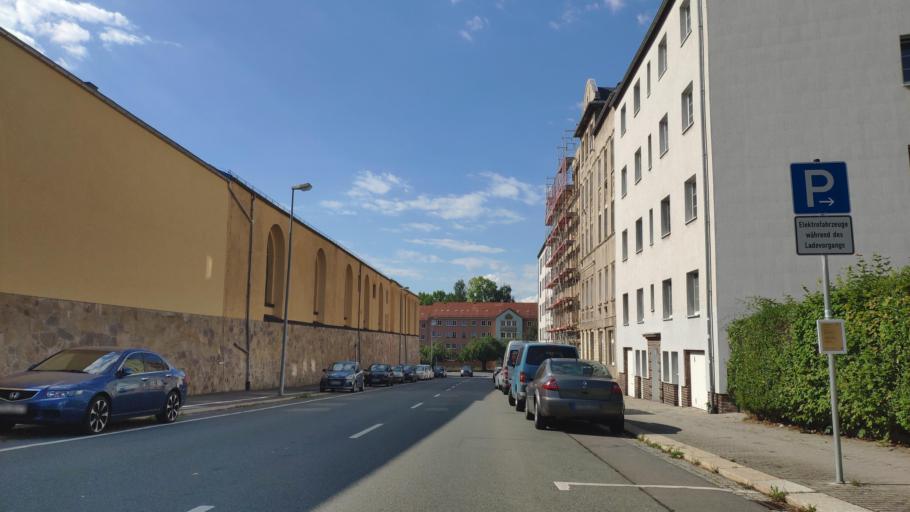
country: DE
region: Saxony
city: Chemnitz
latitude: 50.8240
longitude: 12.9357
